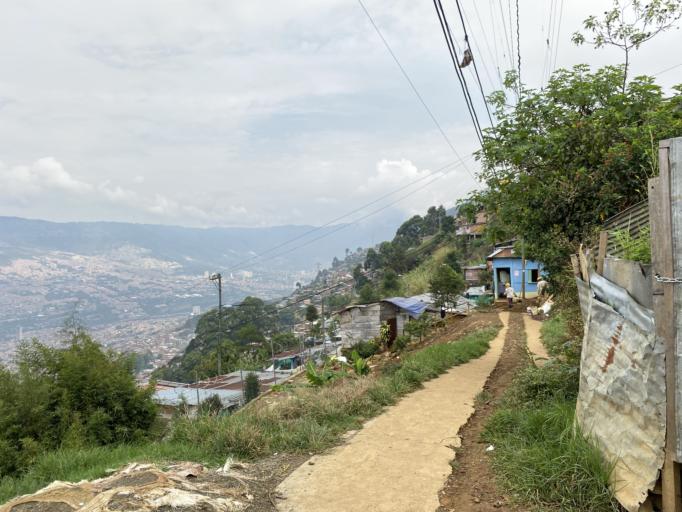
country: CO
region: Antioquia
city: Medellin
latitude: 6.2641
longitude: -75.5397
